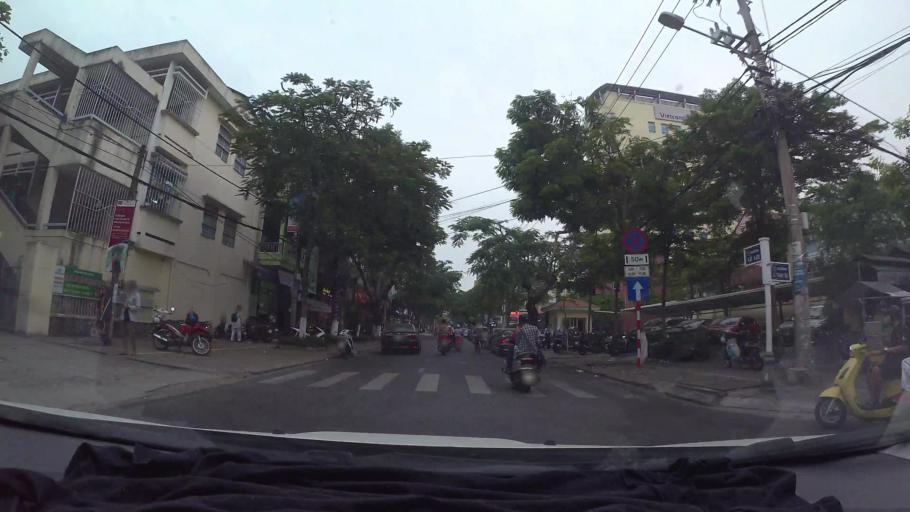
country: VN
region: Da Nang
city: Da Nang
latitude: 16.0738
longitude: 108.2201
